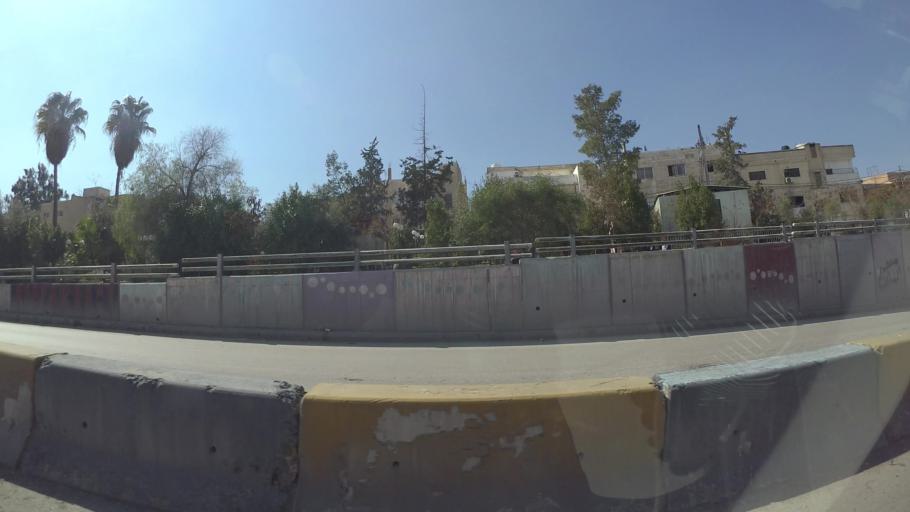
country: JO
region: Zarqa
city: Zarqa
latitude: 32.0714
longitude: 36.0982
